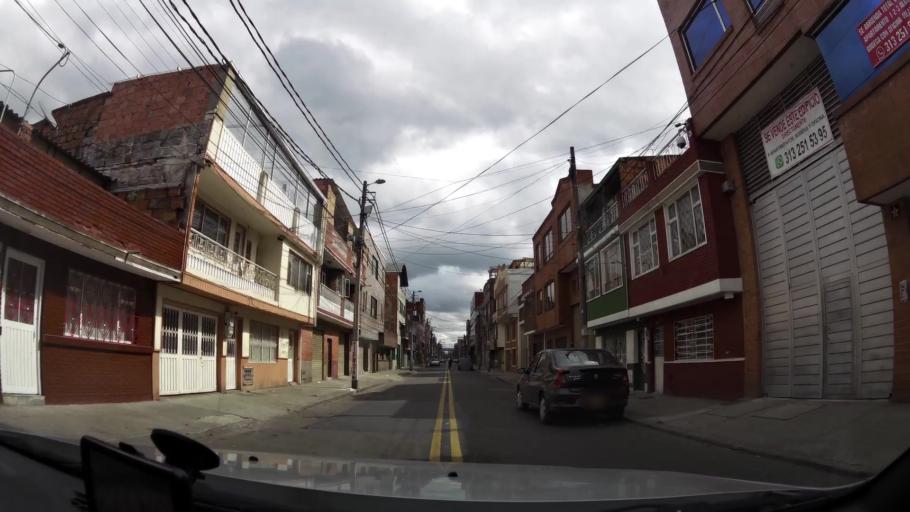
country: CO
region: Bogota D.C.
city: Bogota
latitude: 4.6236
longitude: -74.1206
